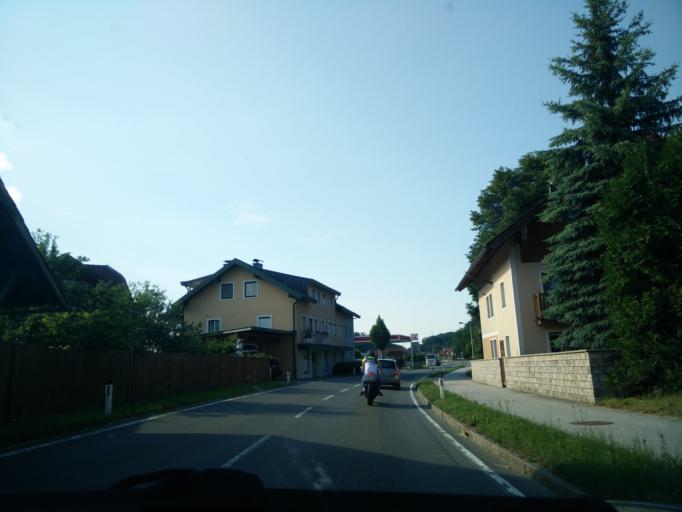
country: AT
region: Salzburg
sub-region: Politischer Bezirk Salzburg-Umgebung
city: Elsbethen
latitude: 47.7540
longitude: 13.0877
